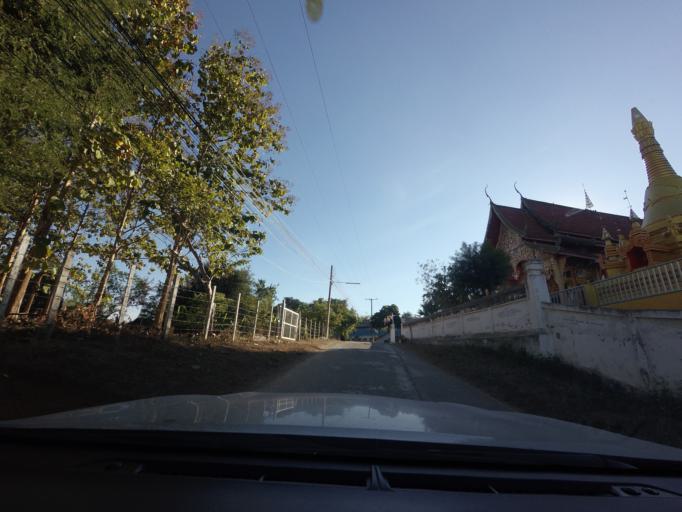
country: TH
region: Mae Hong Son
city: Wiang Nuea
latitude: 19.3950
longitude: 98.4218
